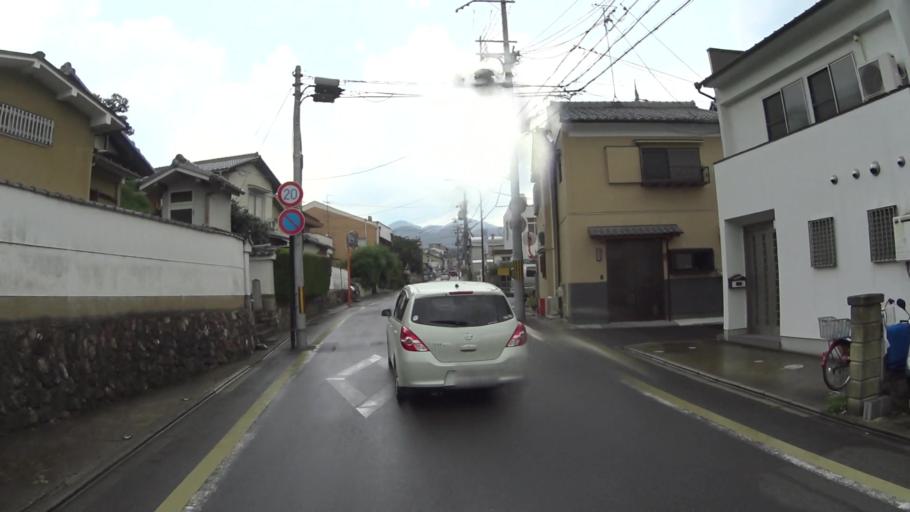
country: JP
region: Kyoto
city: Kyoto
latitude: 35.0234
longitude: 135.7159
